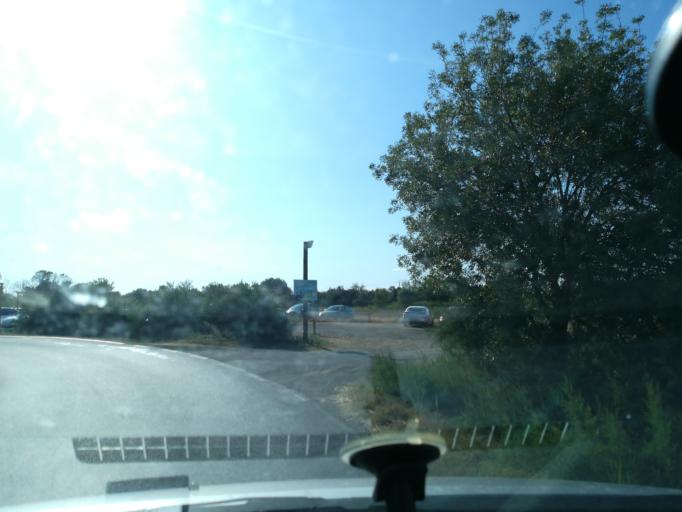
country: FR
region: Languedoc-Roussillon
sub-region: Departement de l'Herault
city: Vias
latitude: 43.2970
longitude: 3.3998
